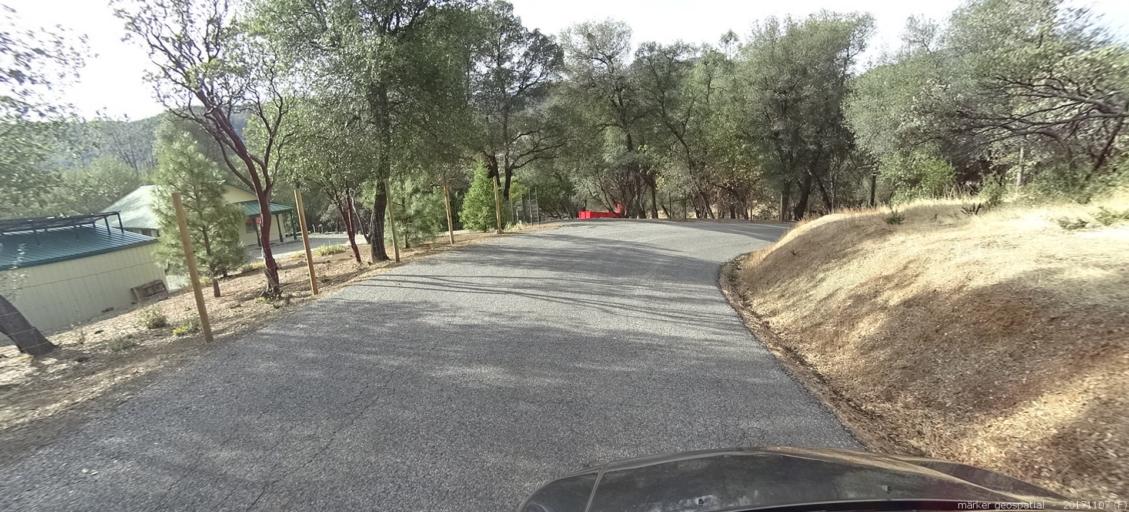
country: US
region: California
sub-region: Shasta County
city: Shasta
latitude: 40.5329
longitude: -122.5267
